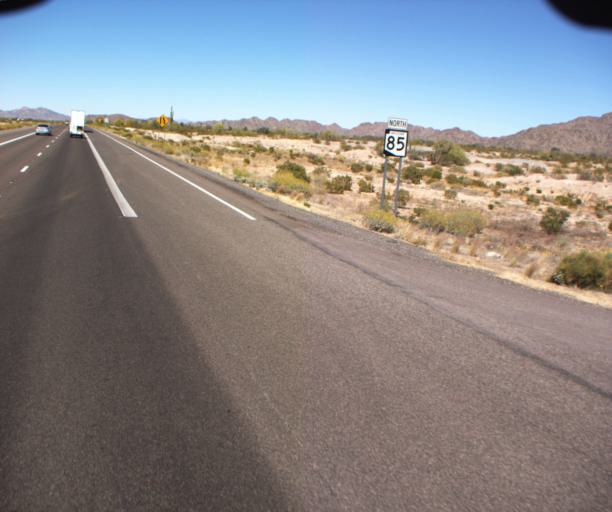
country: US
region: Arizona
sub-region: Maricopa County
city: Gila Bend
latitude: 33.1311
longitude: -112.6501
